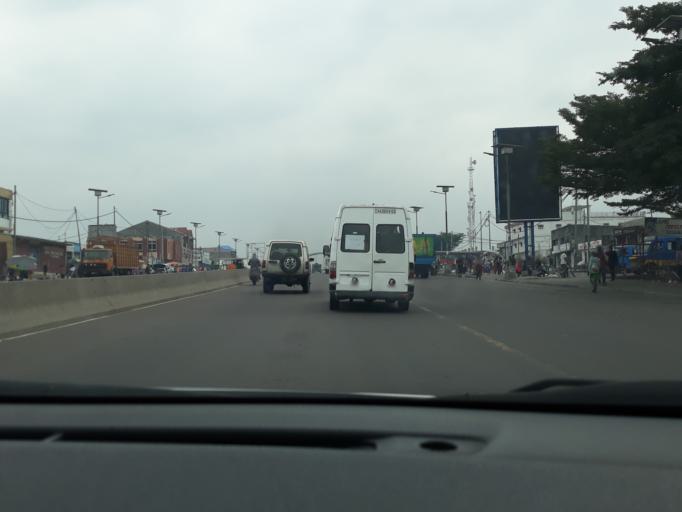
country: CD
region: Kinshasa
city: Masina
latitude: -4.3955
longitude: 15.3881
